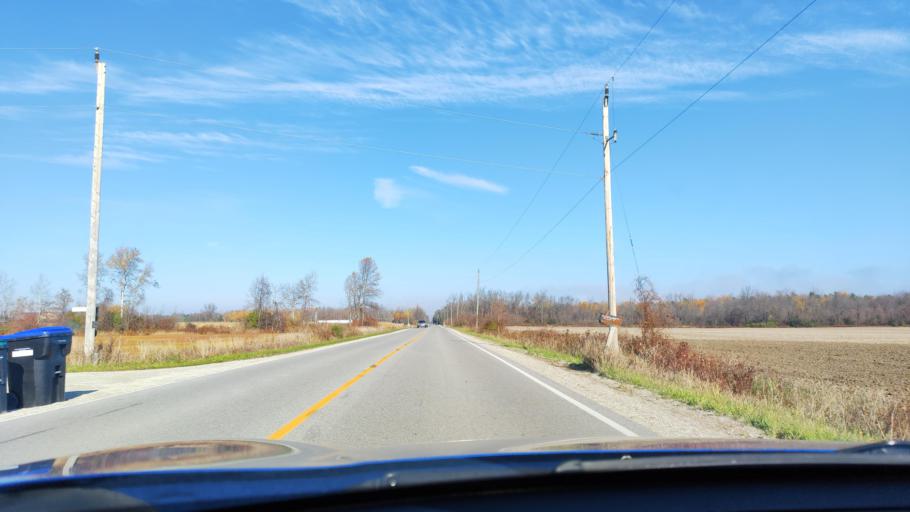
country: CA
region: Ontario
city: Wasaga Beach
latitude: 44.3996
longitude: -80.0577
